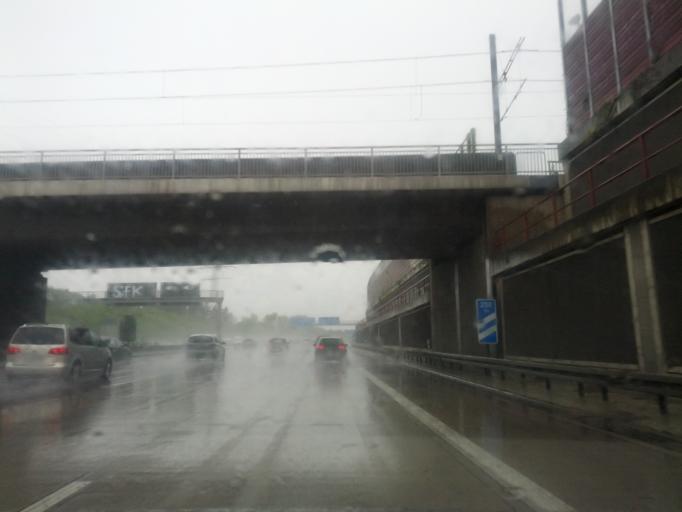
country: DE
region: North Rhine-Westphalia
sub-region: Regierungsbezirk Koln
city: Merheim
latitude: 50.9422
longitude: 7.0421
